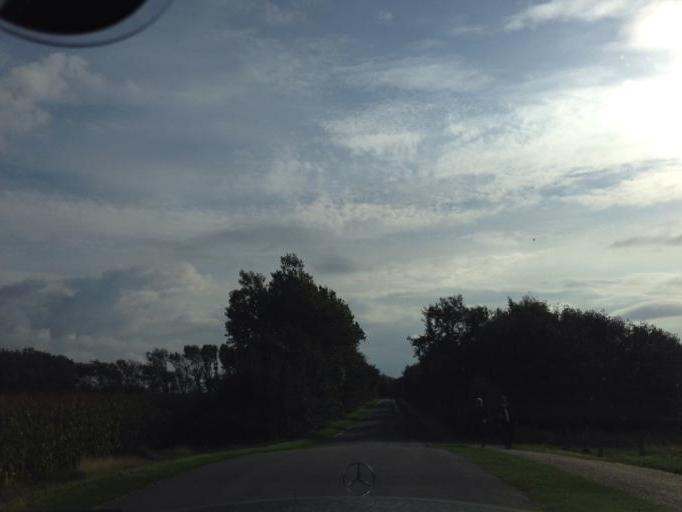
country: DE
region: Schleswig-Holstein
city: Nieblum
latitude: 54.6837
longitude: 8.4919
